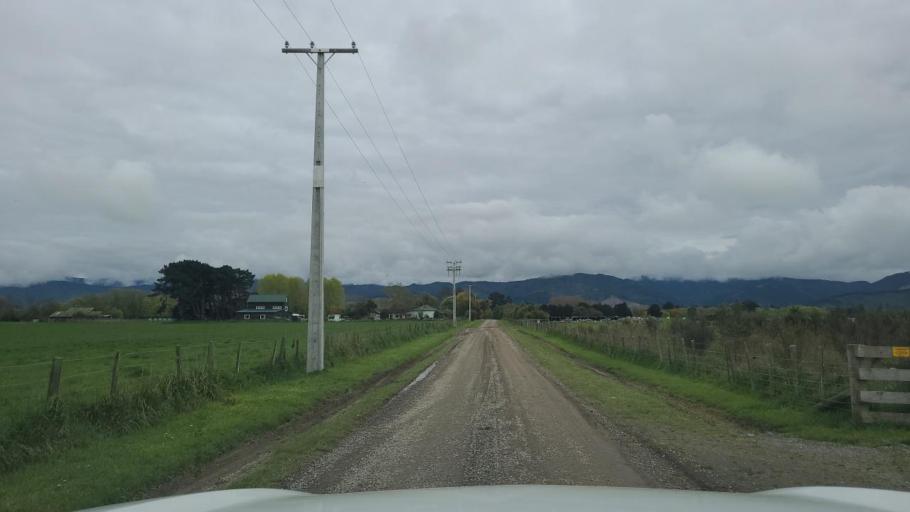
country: NZ
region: Wellington
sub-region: Masterton District
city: Masterton
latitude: -41.0505
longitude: 175.4979
